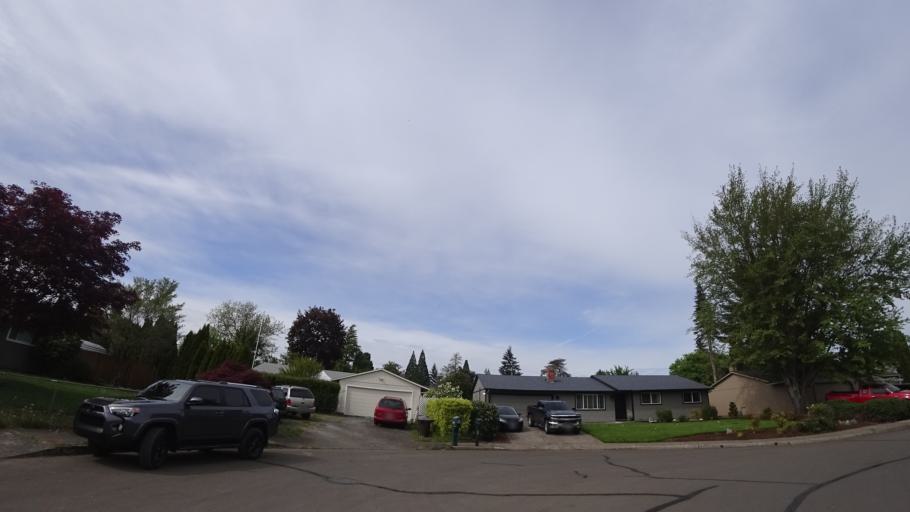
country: US
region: Oregon
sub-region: Washington County
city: Hillsboro
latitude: 45.5184
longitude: -122.9458
